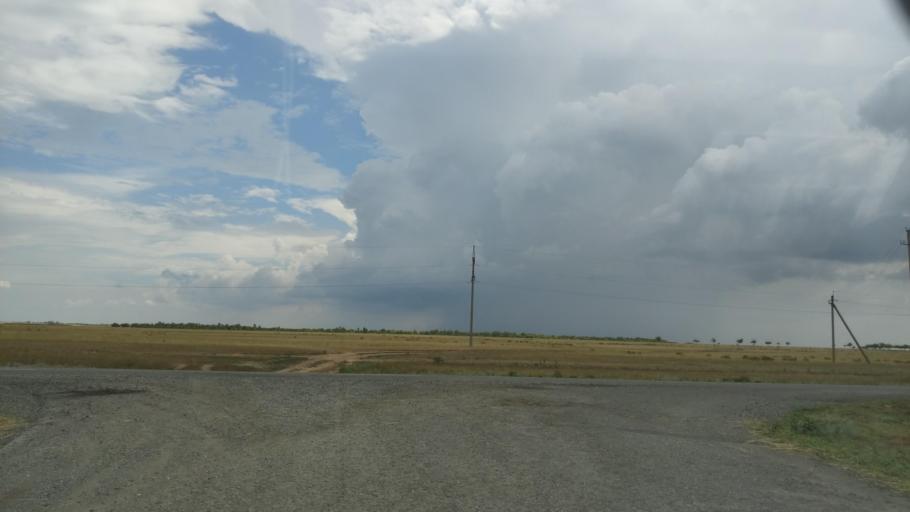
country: KZ
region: Pavlodar
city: Pavlodar
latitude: 52.6328
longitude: 77.3478
